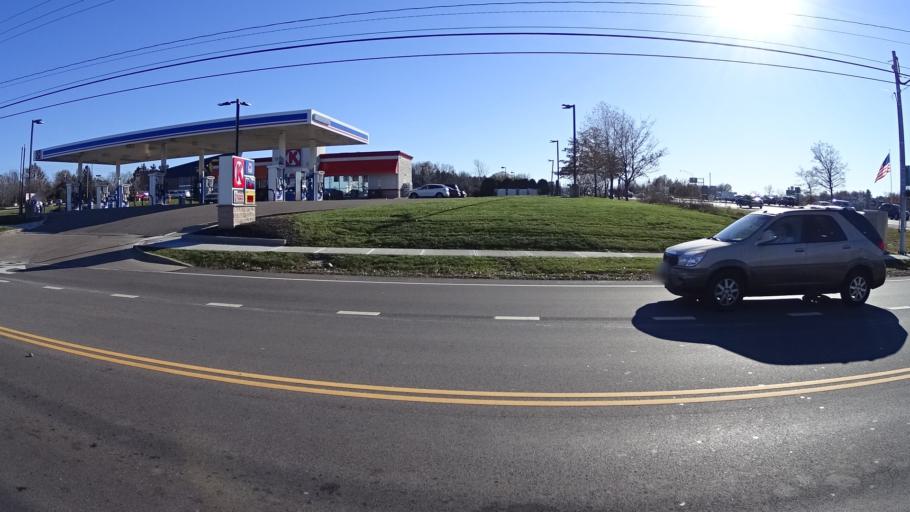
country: US
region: Ohio
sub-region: Lorain County
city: Avon Center
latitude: 41.4672
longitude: -82.0213
